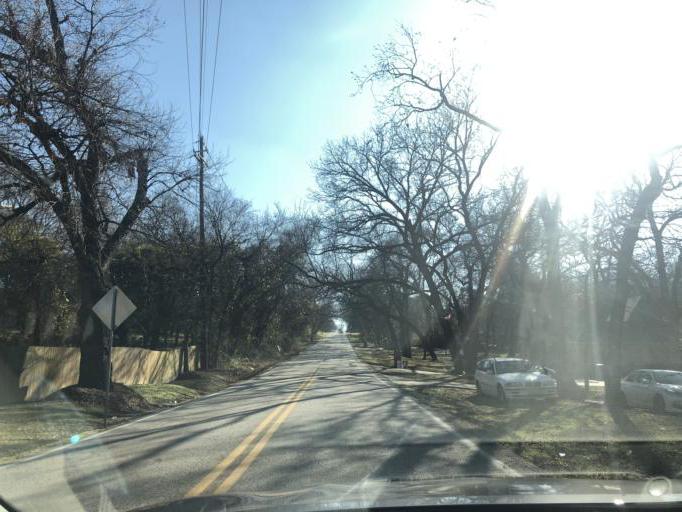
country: US
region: Texas
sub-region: Dallas County
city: Duncanville
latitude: 32.6236
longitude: -96.9254
